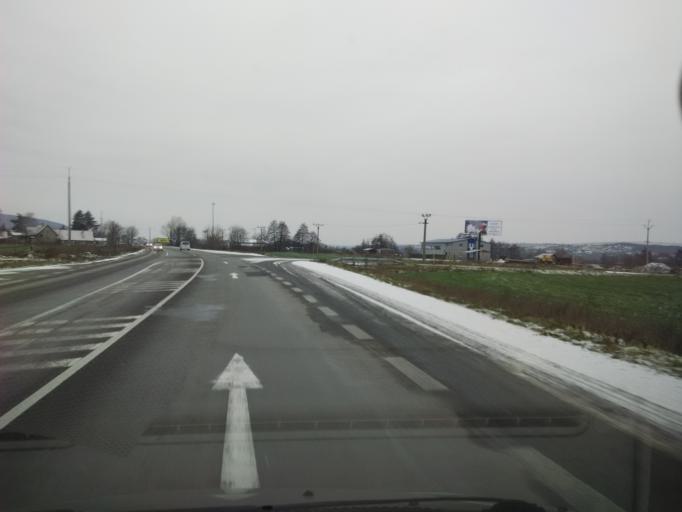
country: SK
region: Nitriansky
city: Partizanske
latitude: 48.6261
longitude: 18.4343
